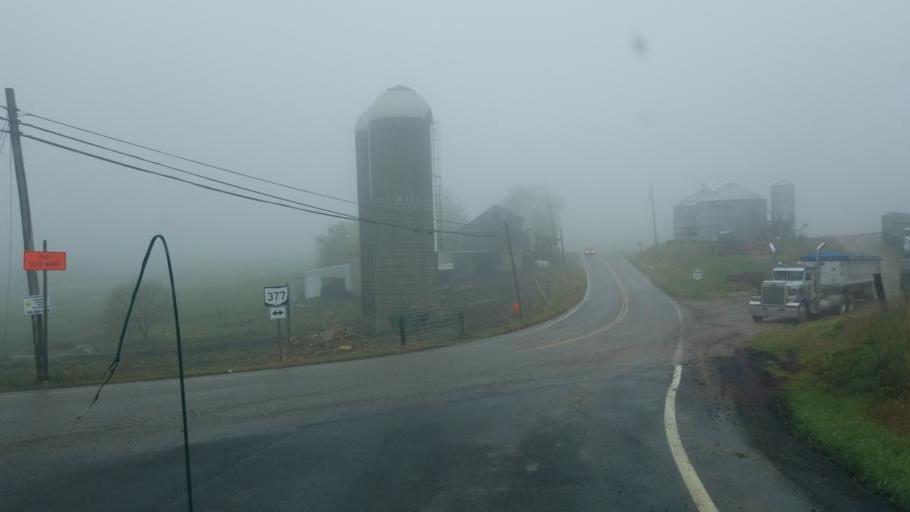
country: US
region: Ohio
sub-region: Morgan County
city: McConnelsville
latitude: 39.5687
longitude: -81.8477
